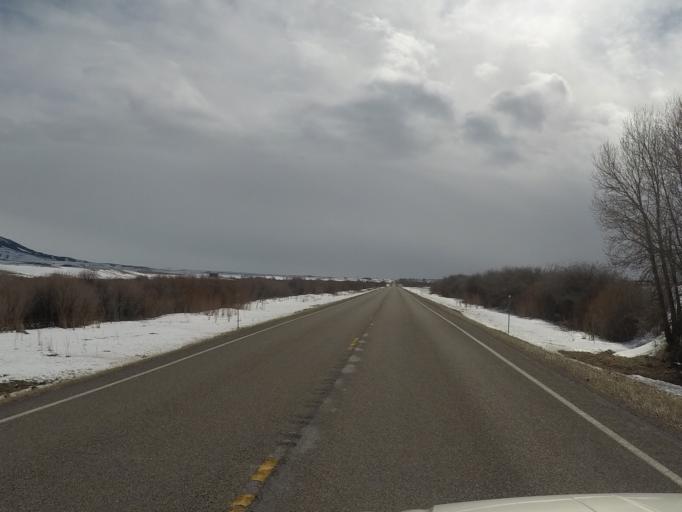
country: US
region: Montana
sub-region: Meagher County
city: White Sulphur Springs
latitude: 46.5786
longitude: -110.8471
